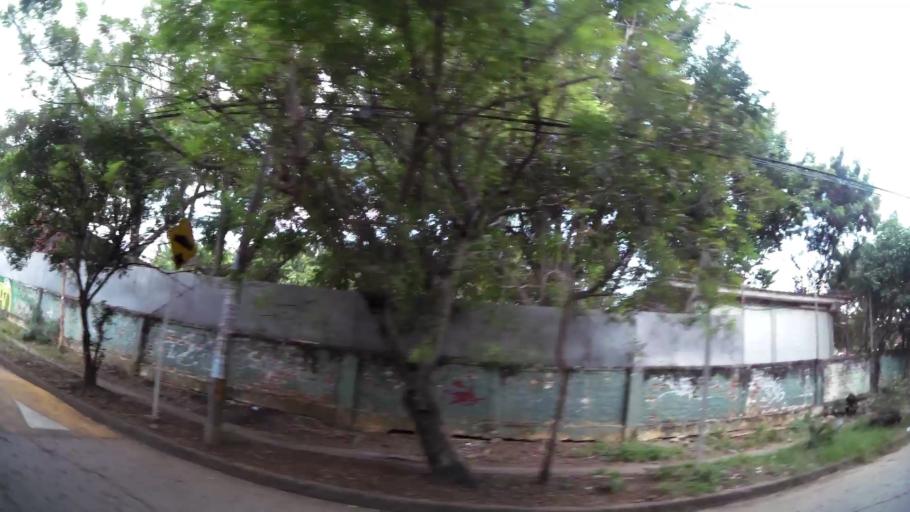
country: CO
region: Valle del Cauca
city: Cali
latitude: 3.4110
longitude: -76.5200
